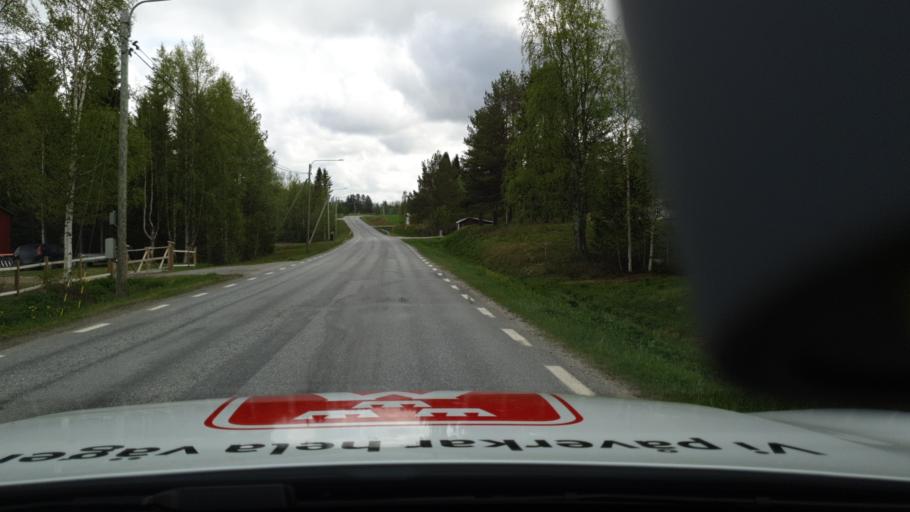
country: SE
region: Vaesterbotten
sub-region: Vilhelmina Kommun
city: Sjoberg
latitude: 64.6449
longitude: 16.3513
